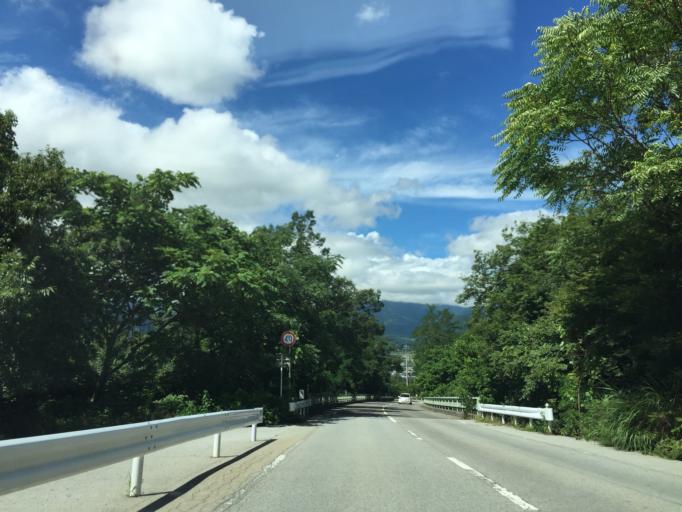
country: JP
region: Yamanashi
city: Nirasaki
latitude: 35.7868
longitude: 138.3946
